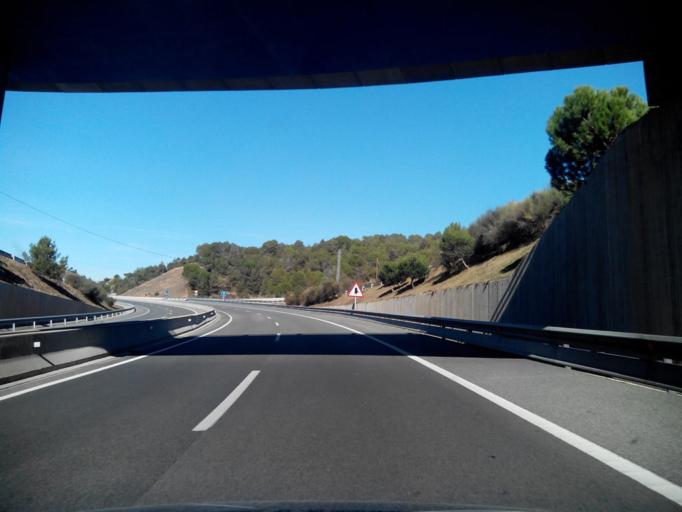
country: ES
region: Catalonia
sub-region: Provincia de Barcelona
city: Balsareny
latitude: 41.8718
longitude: 1.8761
